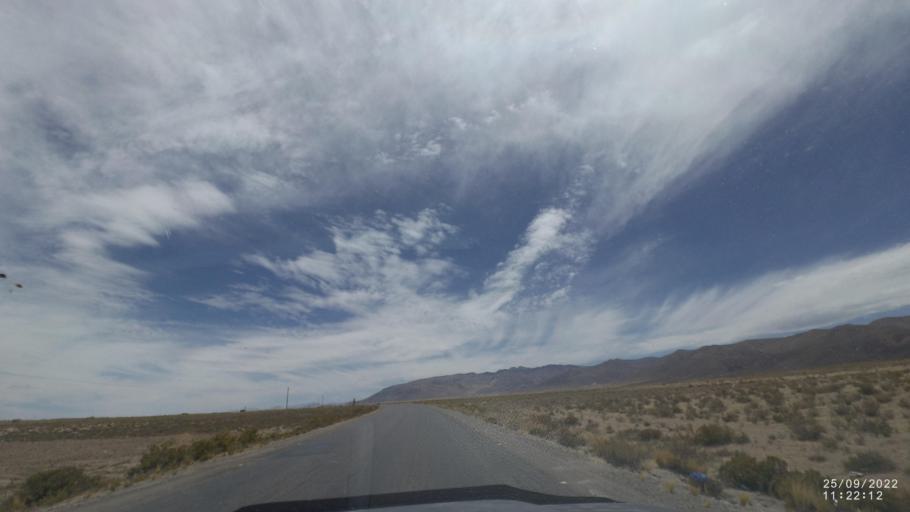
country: BO
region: Oruro
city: Challapata
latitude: -19.1298
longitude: -66.7684
